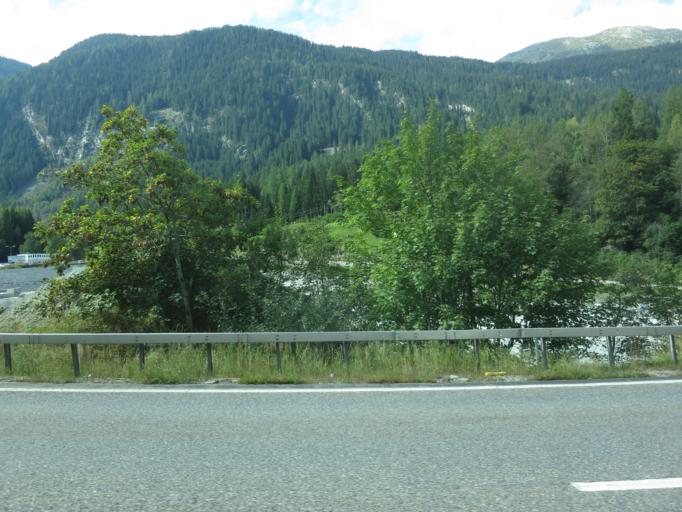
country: CH
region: Grisons
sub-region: Hinterrhein District
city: Thusis
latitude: 46.5918
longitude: 9.4279
